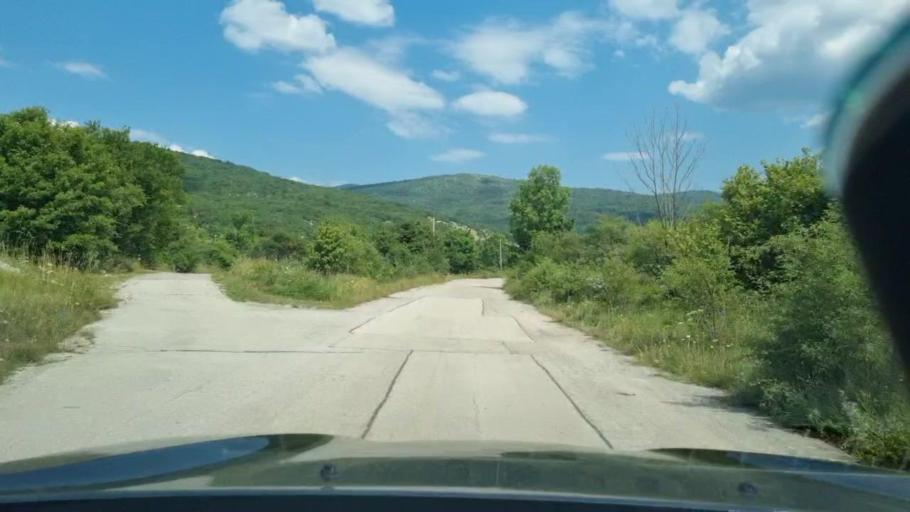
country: BA
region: Federation of Bosnia and Herzegovina
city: Bosansko Grahovo
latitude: 44.2956
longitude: 16.2997
